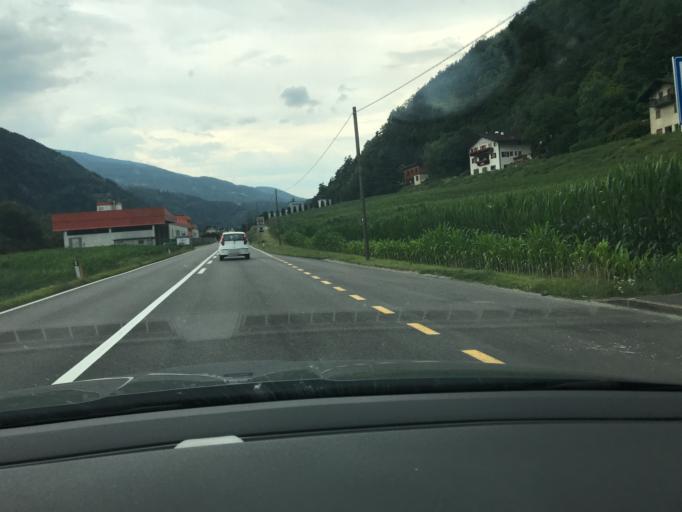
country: IT
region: Trentino-Alto Adige
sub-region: Bolzano
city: Velturno
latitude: 46.6766
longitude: 11.6204
